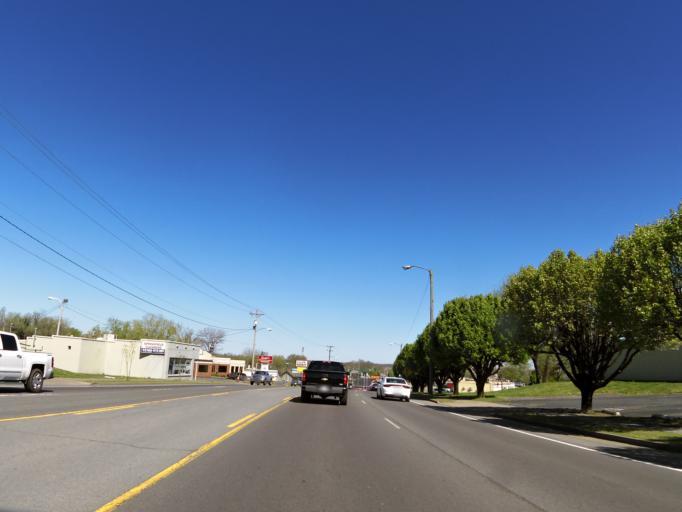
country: US
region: Tennessee
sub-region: Robertson County
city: Springfield
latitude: 36.4963
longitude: -86.8810
